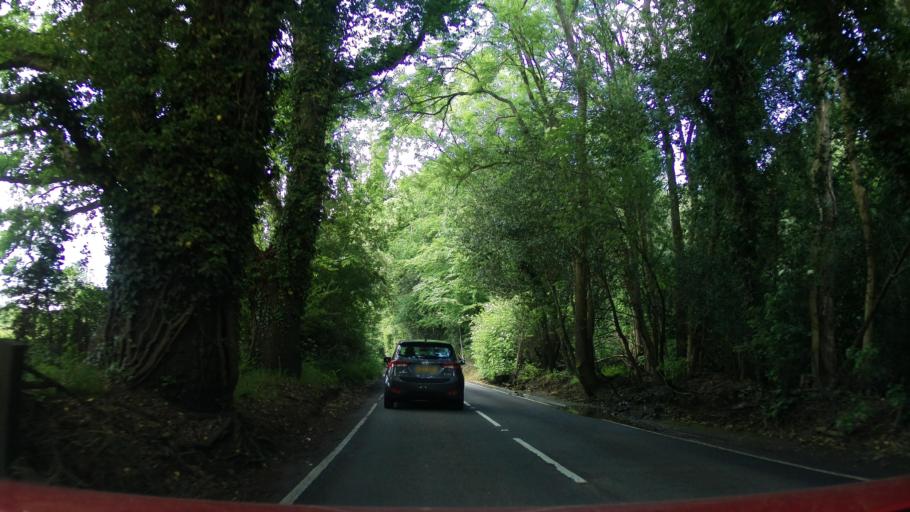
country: GB
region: England
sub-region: Hertfordshire
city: Chorleywood
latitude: 51.6681
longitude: -0.4638
